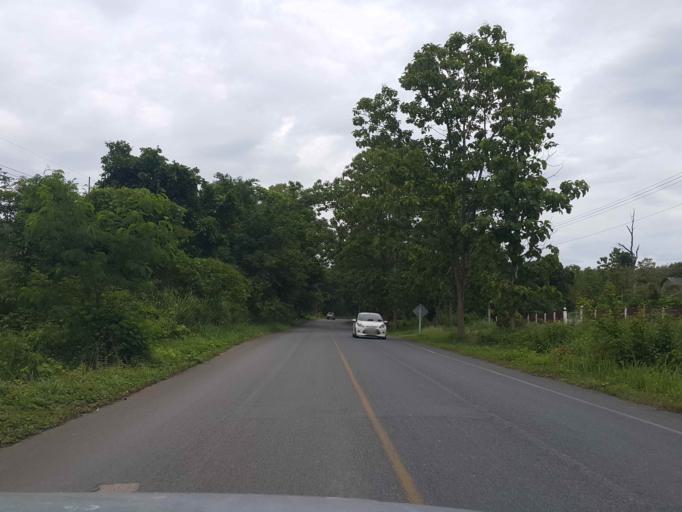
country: TH
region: Lampang
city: Thoen
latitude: 17.6012
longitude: 99.3284
